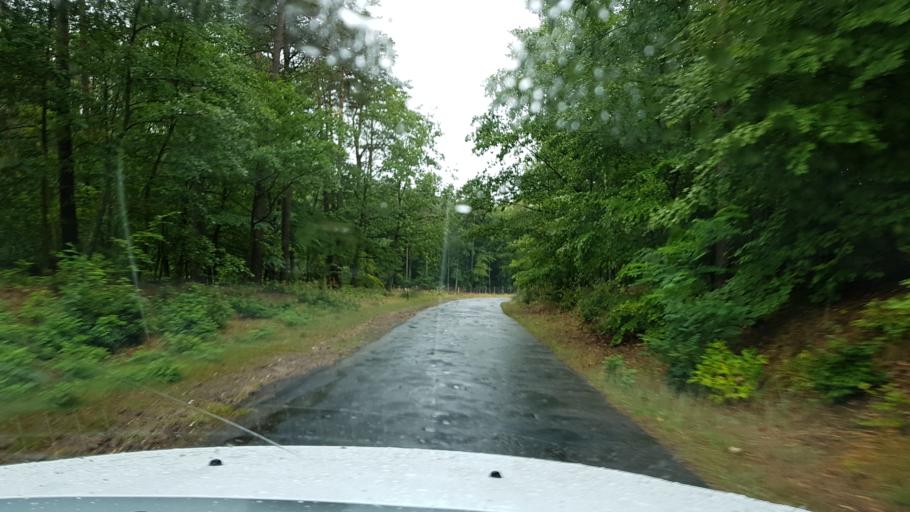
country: DE
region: Brandenburg
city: Meyenburg
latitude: 52.9774
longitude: 14.2517
